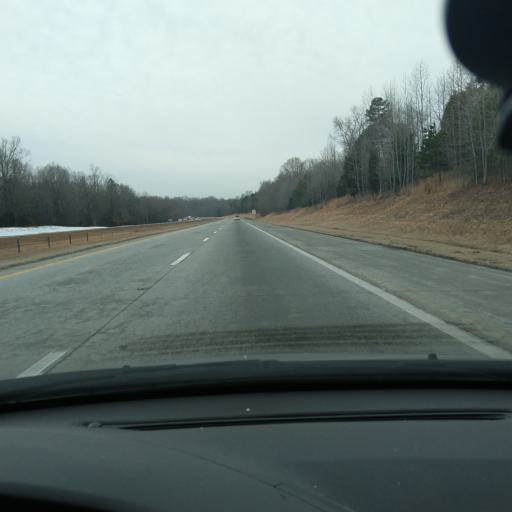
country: US
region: North Carolina
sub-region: Davidson County
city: Welcome
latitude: 35.8717
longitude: -80.2560
